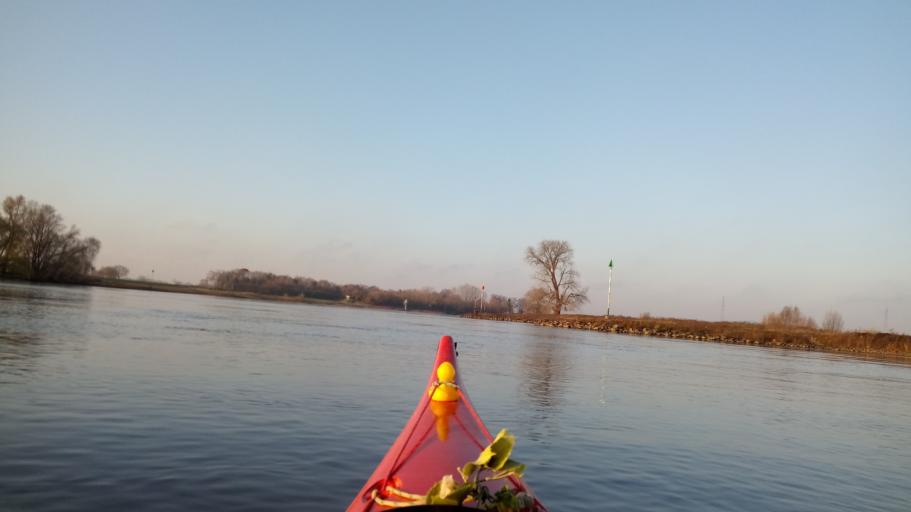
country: NL
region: Gelderland
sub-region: Gemeente Zutphen
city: Zutphen
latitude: 52.1489
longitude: 6.1847
